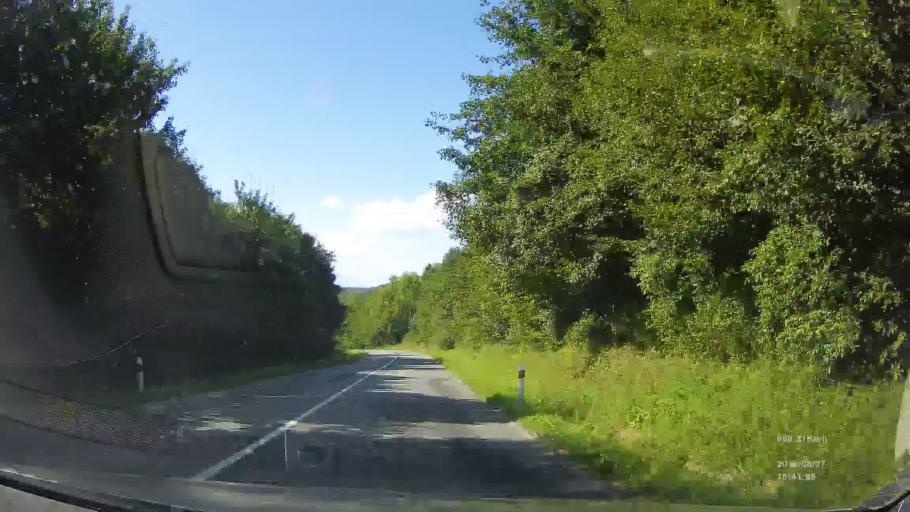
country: SK
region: Presovsky
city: Giraltovce
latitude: 49.1222
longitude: 21.5824
